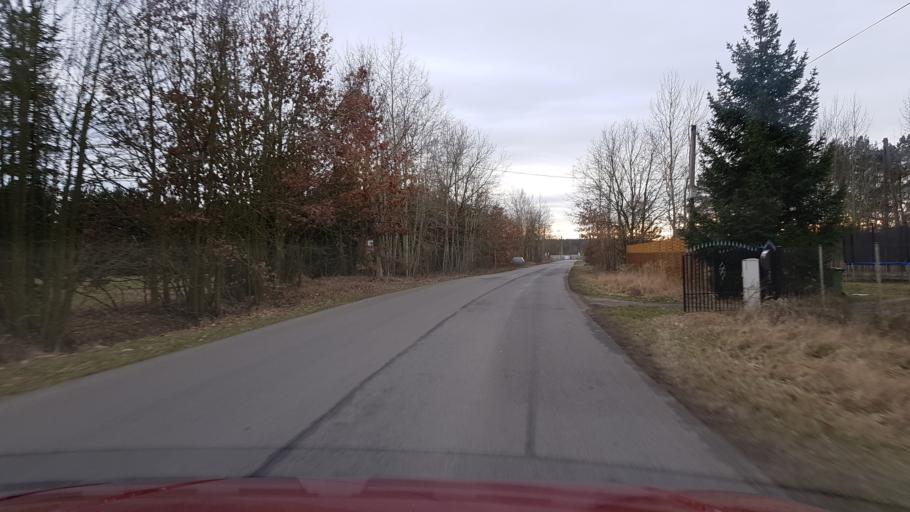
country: PL
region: West Pomeranian Voivodeship
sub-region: Powiat policki
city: Dobra
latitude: 53.5516
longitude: 14.4609
